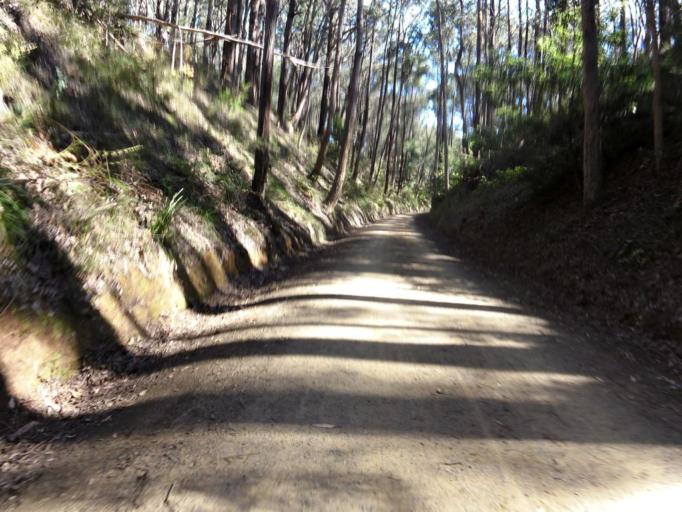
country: AU
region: Victoria
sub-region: Latrobe
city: Moe
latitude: -38.3981
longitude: 146.1748
